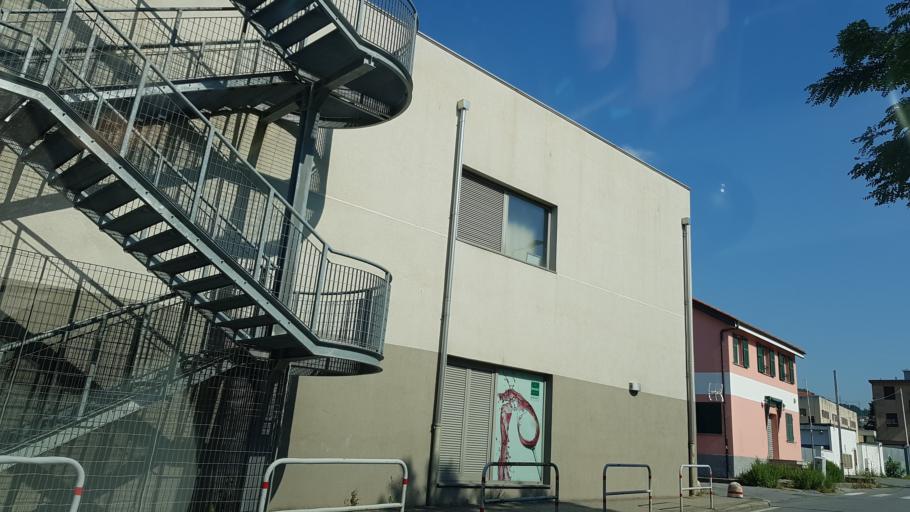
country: IT
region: Liguria
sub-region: Provincia di Genova
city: Manesseno
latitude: 44.4852
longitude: 8.9213
